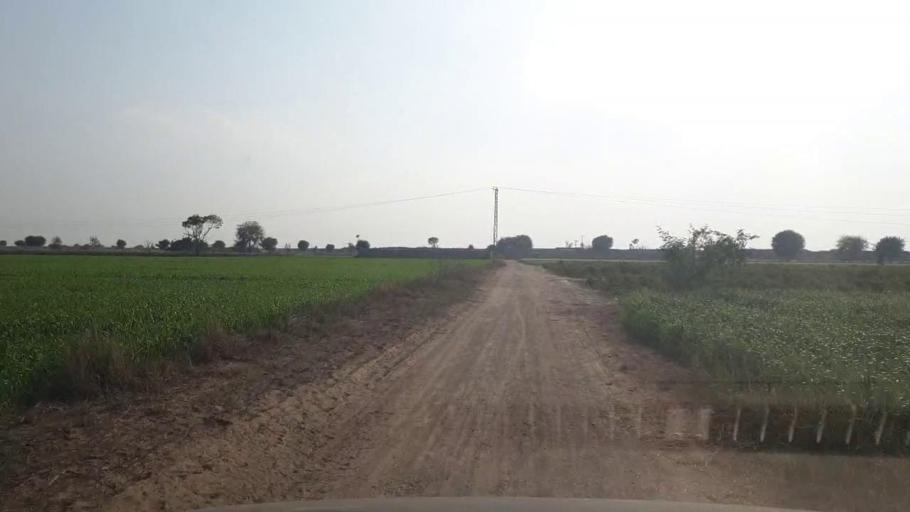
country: PK
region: Sindh
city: Hala
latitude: 25.8452
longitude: 68.3899
